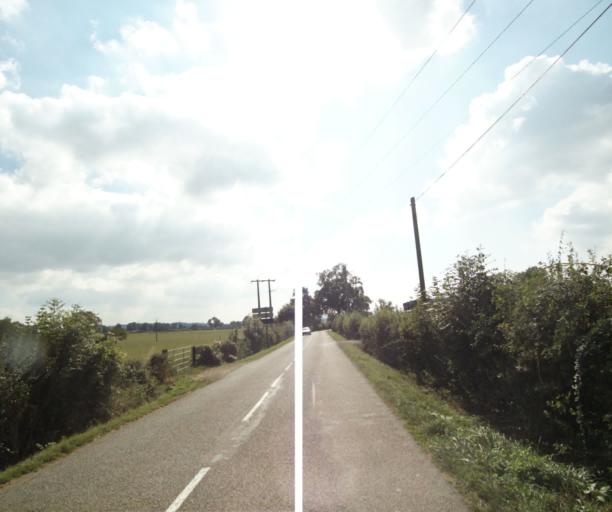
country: FR
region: Bourgogne
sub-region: Departement de Saone-et-Loire
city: Charolles
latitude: 46.3778
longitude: 4.2494
